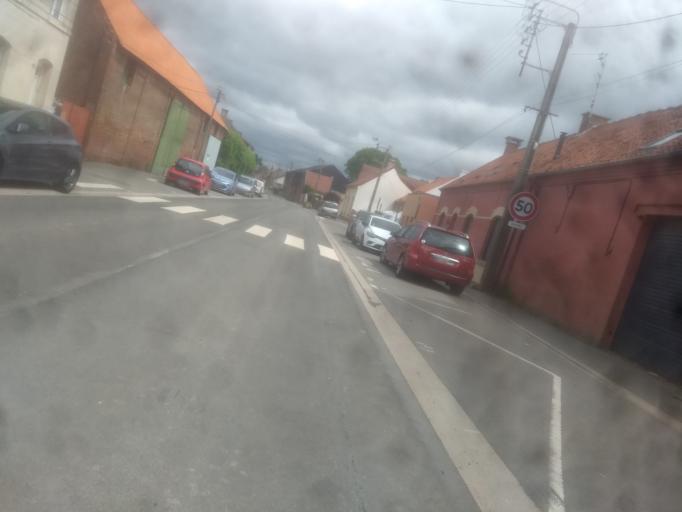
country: FR
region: Nord-Pas-de-Calais
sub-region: Departement du Pas-de-Calais
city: Thelus
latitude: 50.3553
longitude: 2.7946
